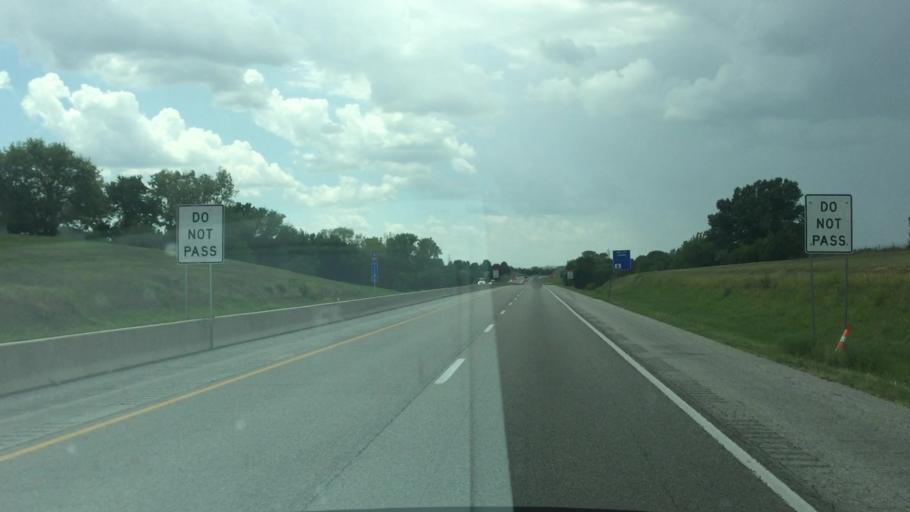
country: US
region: Kansas
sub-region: Shawnee County
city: Topeka
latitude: 38.9970
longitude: -95.6662
